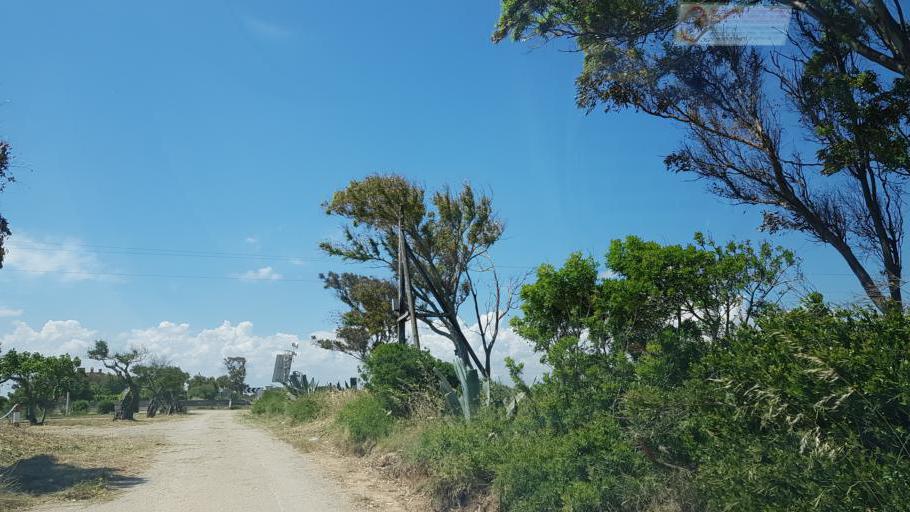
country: IT
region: Apulia
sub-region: Provincia di Brindisi
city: San Vito dei Normanni
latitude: 40.6936
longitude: 17.8191
